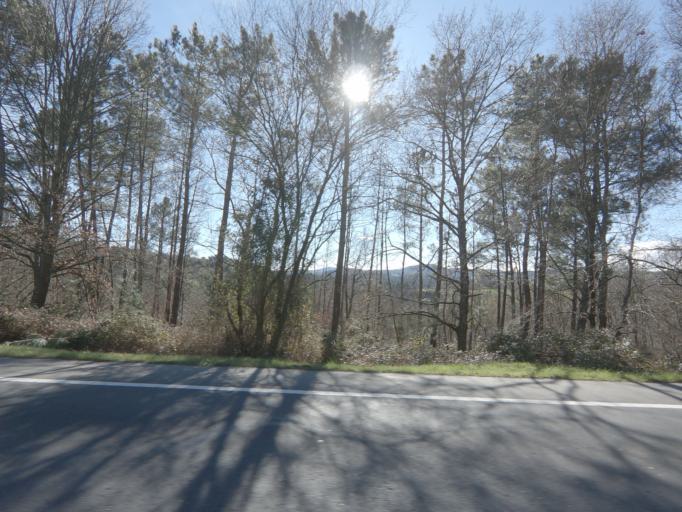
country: ES
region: Galicia
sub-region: Provincia de Pontevedra
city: Silleda
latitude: 42.6863
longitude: -8.2033
